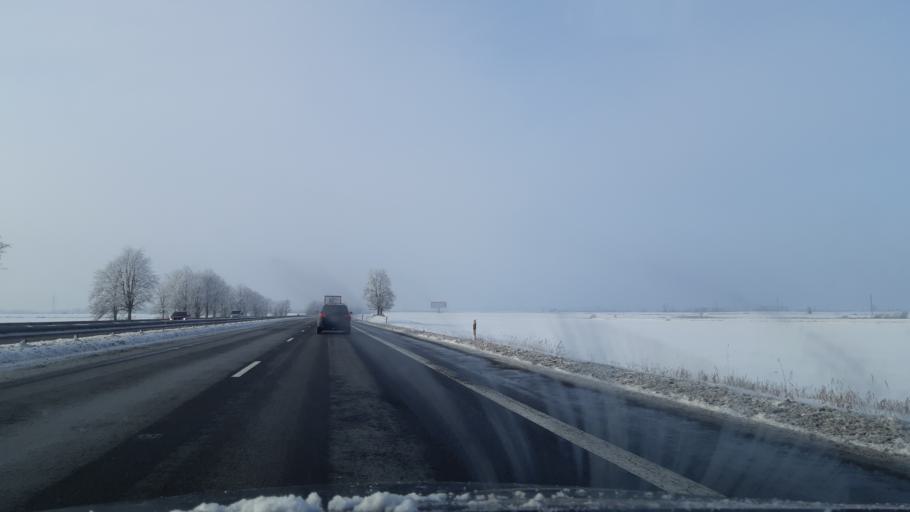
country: LT
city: Kaisiadorys
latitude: 54.8586
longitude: 24.2781
